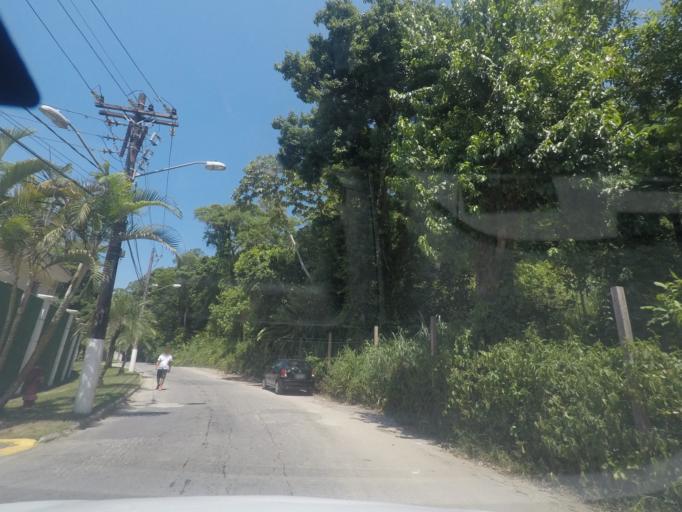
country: BR
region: Rio de Janeiro
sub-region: Nilopolis
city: Nilopolis
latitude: -22.9779
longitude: -43.4549
